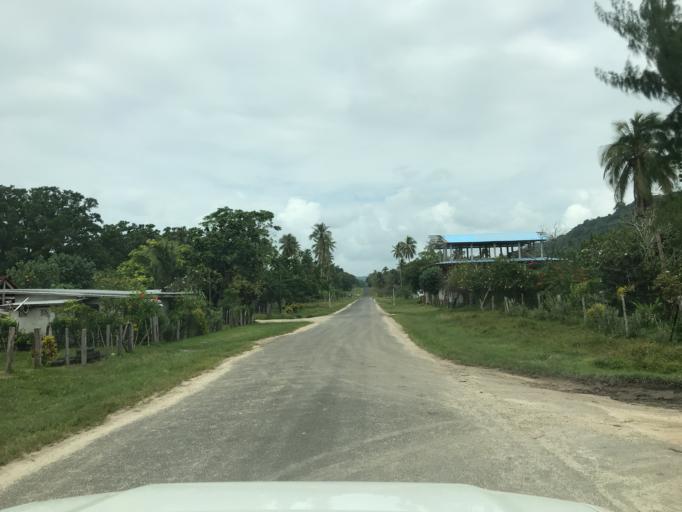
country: VU
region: Sanma
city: Port-Olry
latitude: -15.0436
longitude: 167.0721
